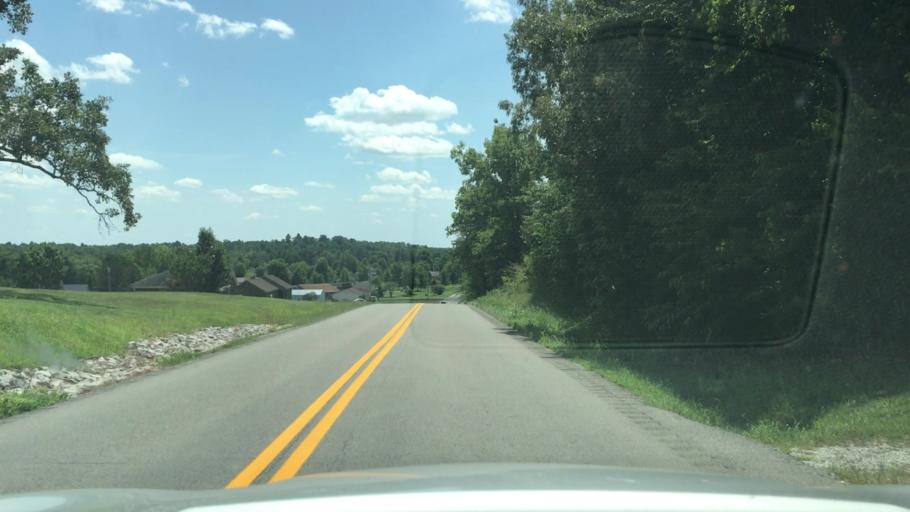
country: US
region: Kentucky
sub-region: Christian County
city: Hopkinsville
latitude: 36.9185
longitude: -87.4386
